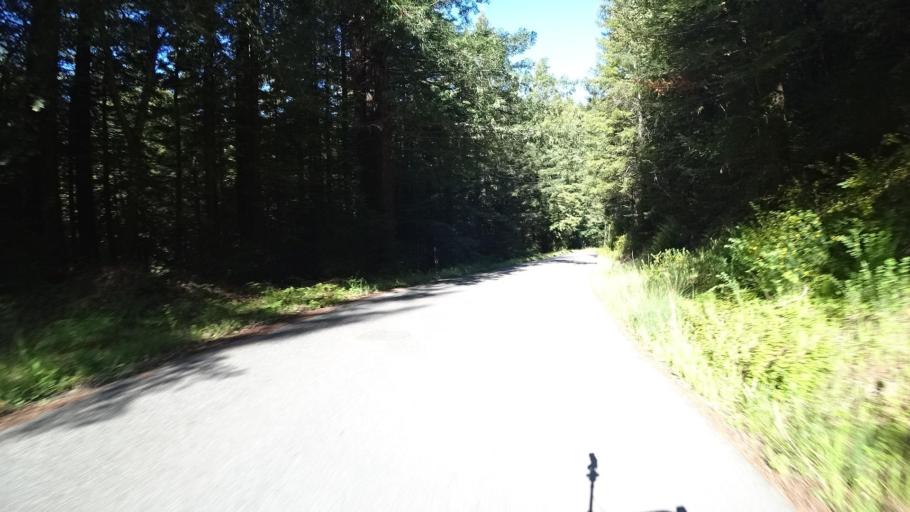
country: US
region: California
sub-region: Humboldt County
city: Rio Dell
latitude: 40.4602
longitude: -123.9989
